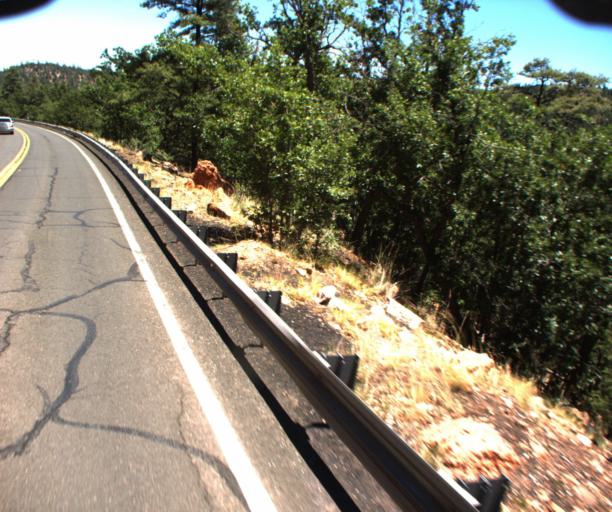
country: US
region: Arizona
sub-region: Gila County
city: Pine
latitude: 34.5944
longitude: -111.2470
